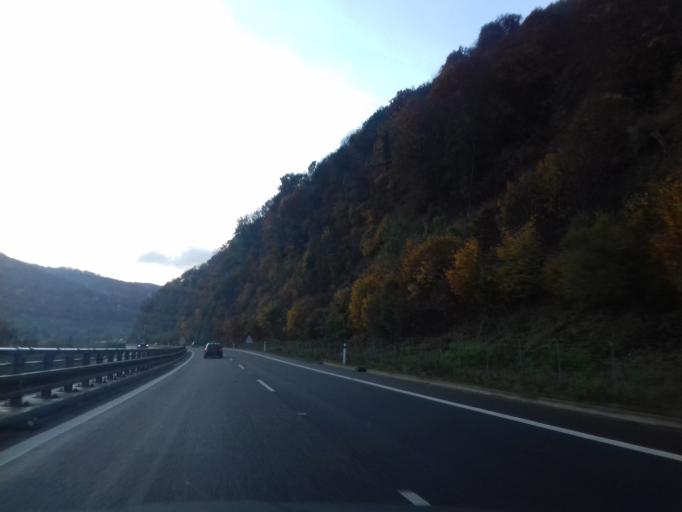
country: SK
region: Banskobystricky
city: Zarnovica
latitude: 48.4504
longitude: 18.6926
